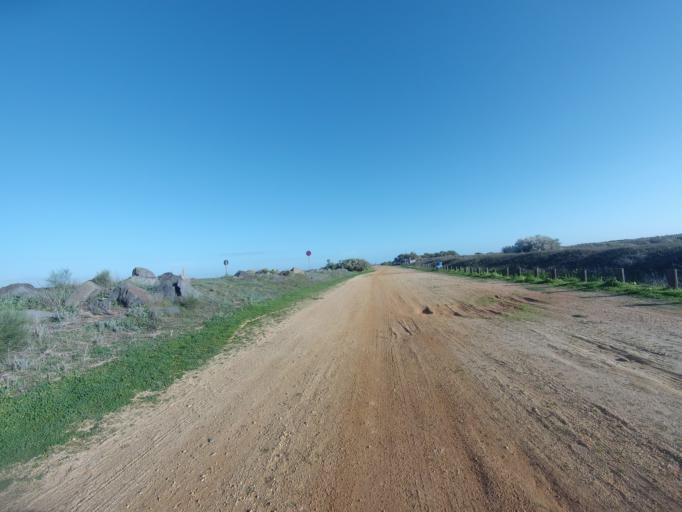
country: ES
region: Andalusia
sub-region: Provincia de Huelva
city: Punta Umbria
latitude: 37.1503
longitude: -6.8969
